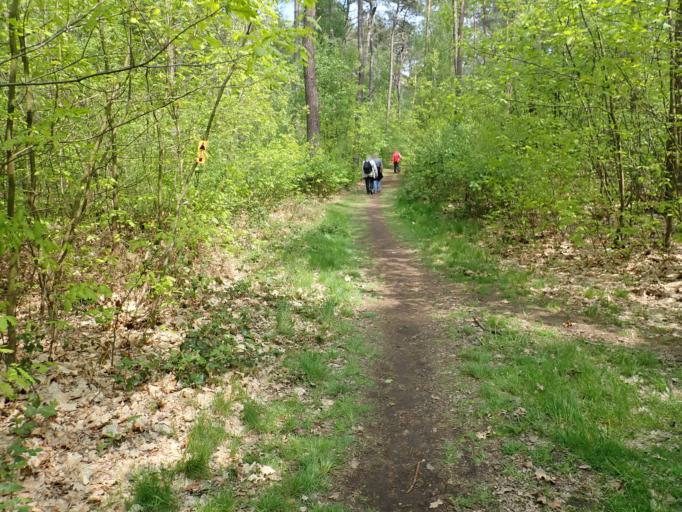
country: BE
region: Flanders
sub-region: Provincie Antwerpen
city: Herentals
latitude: 51.1985
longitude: 4.8374
